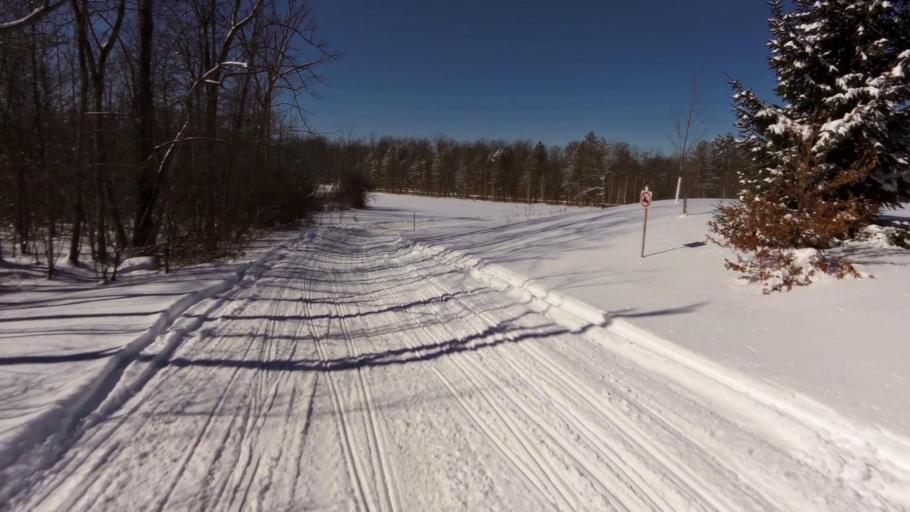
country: US
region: New York
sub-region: Chautauqua County
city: Mayville
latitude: 42.2723
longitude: -79.4581
